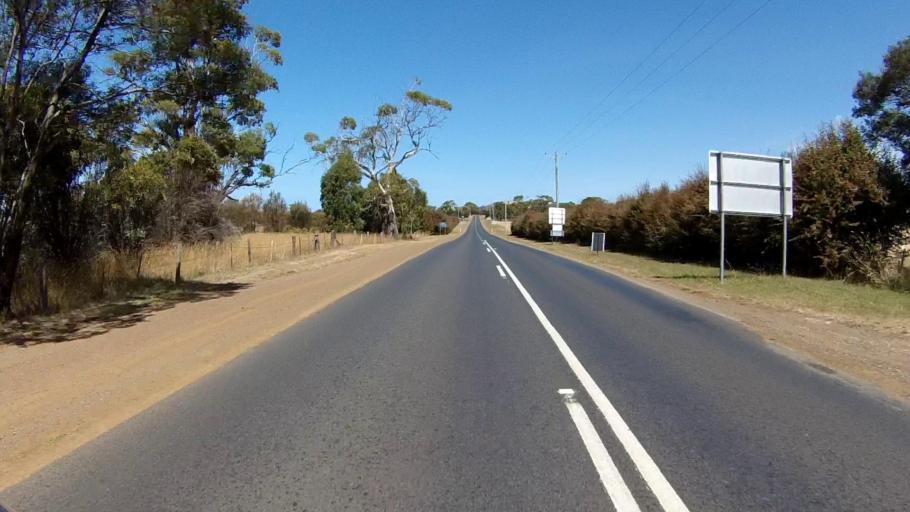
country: AU
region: Tasmania
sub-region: Sorell
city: Sorell
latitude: -42.1345
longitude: 148.0712
